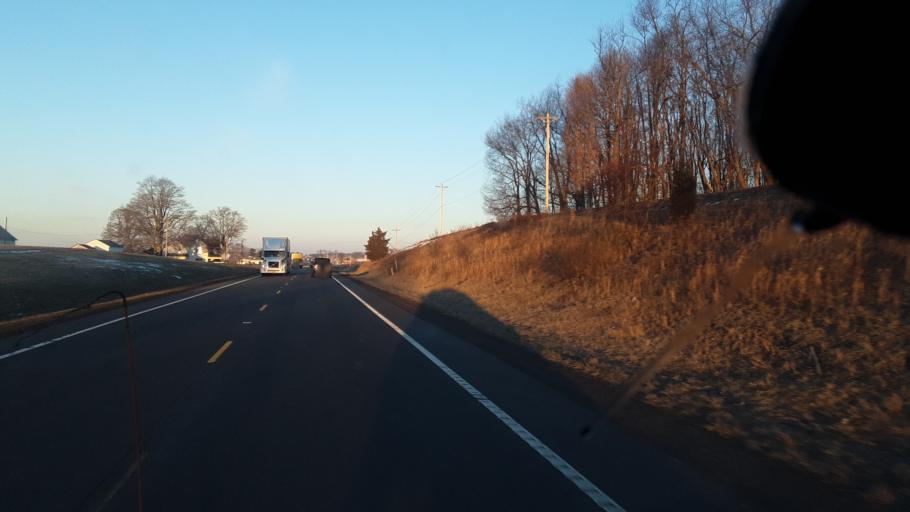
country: US
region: Ohio
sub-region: Perry County
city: Somerset
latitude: 39.8311
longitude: -82.3591
